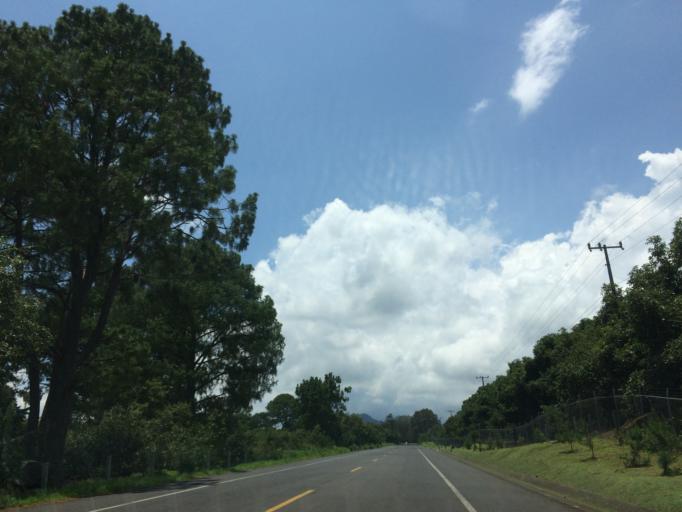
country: MX
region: Michoacan
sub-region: Periban
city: San Francisco Periban
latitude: 19.5541
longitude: -102.3886
